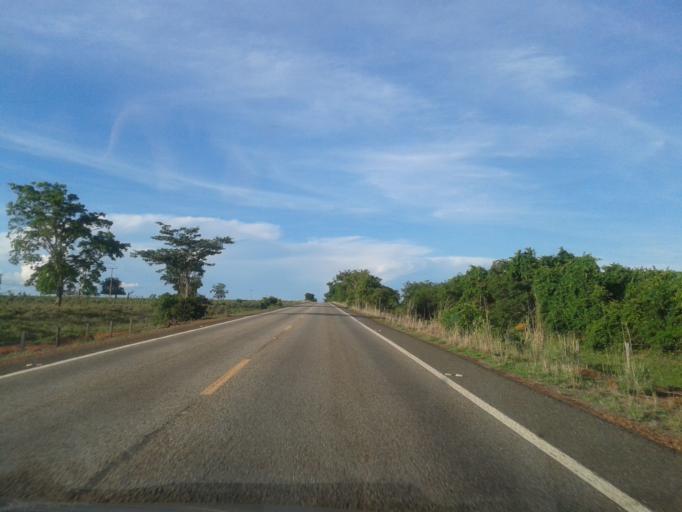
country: BR
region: Goias
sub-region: Sao Miguel Do Araguaia
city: Sao Miguel do Araguaia
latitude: -13.5358
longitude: -50.3062
